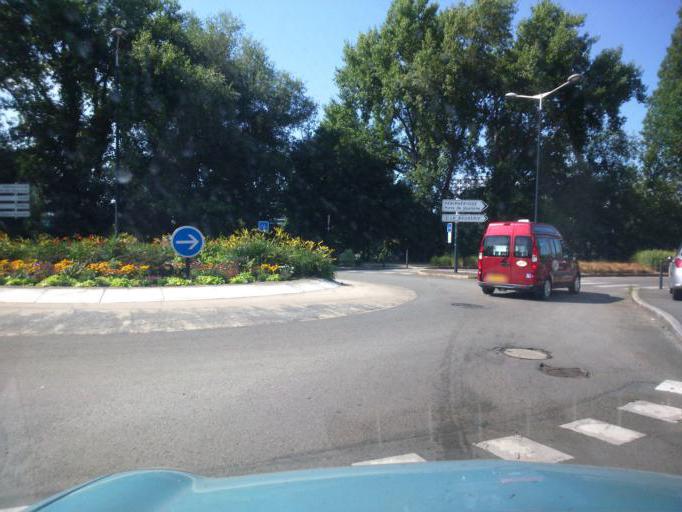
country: FR
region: Pays de la Loire
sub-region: Departement de la Loire-Atlantique
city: Reze
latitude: 47.2006
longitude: -1.5333
